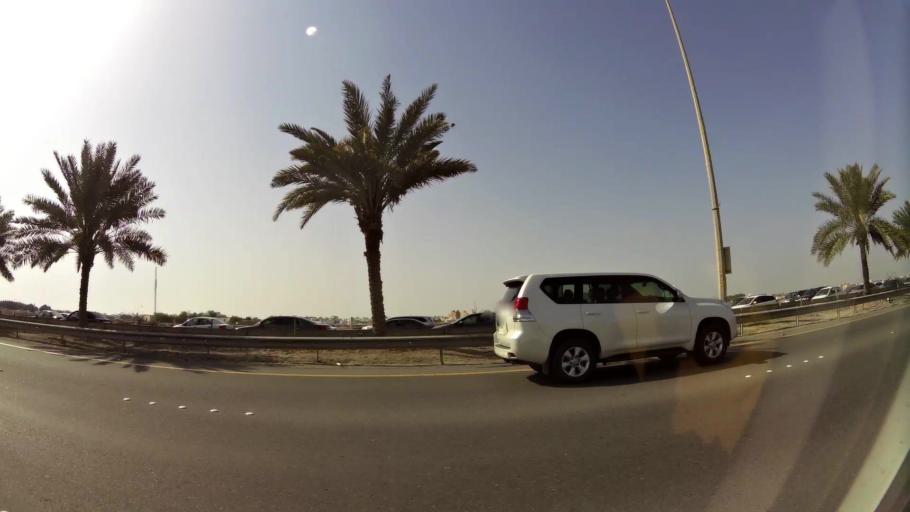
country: BH
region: Manama
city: Jidd Hafs
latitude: 26.2041
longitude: 50.5139
